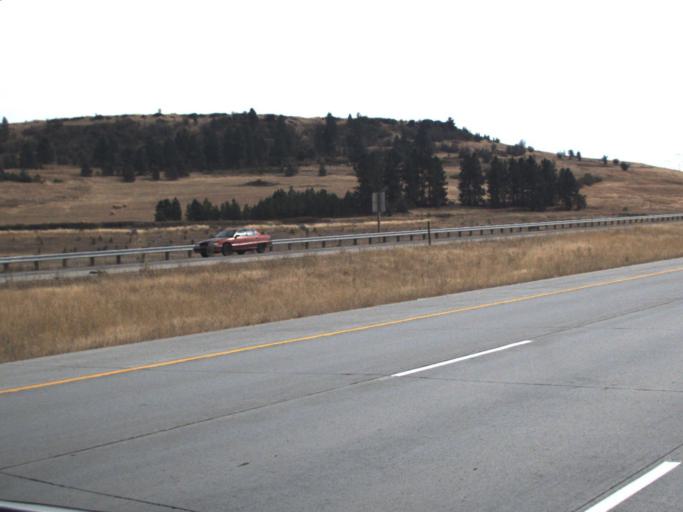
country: US
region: Washington
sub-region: Spokane County
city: Mead
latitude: 47.7476
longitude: -117.3599
